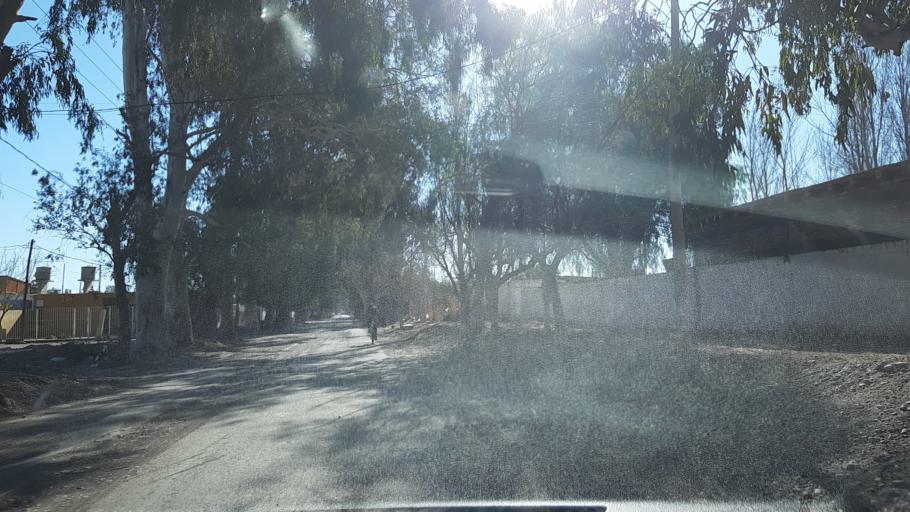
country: AR
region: San Juan
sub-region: Departamento de Zonda
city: Zonda
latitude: -31.5512
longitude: -68.7278
